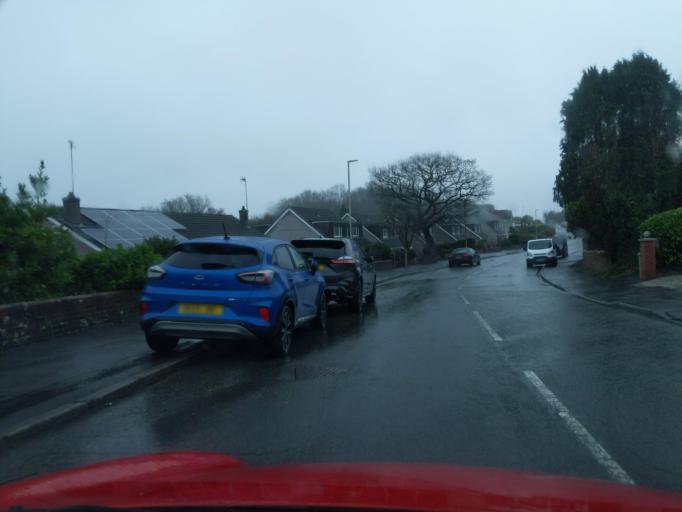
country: GB
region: England
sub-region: Plymouth
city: Plymstock
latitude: 50.4013
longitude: -4.1067
